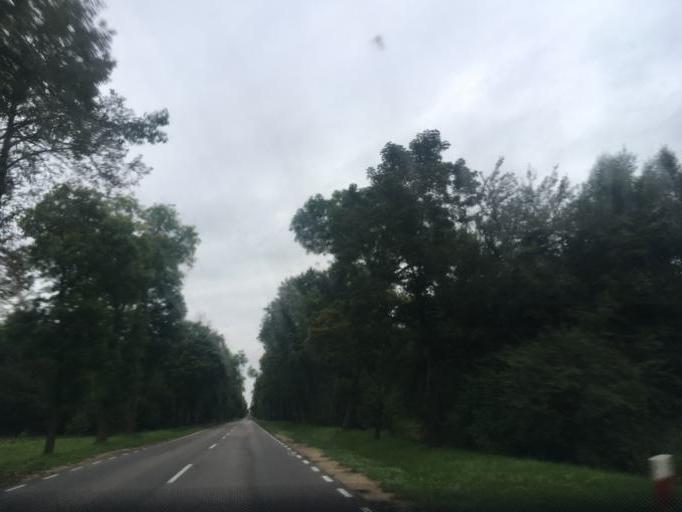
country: PL
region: Podlasie
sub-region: Powiat bielski
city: Bielsk Podlaski
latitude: 52.7557
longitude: 23.1277
